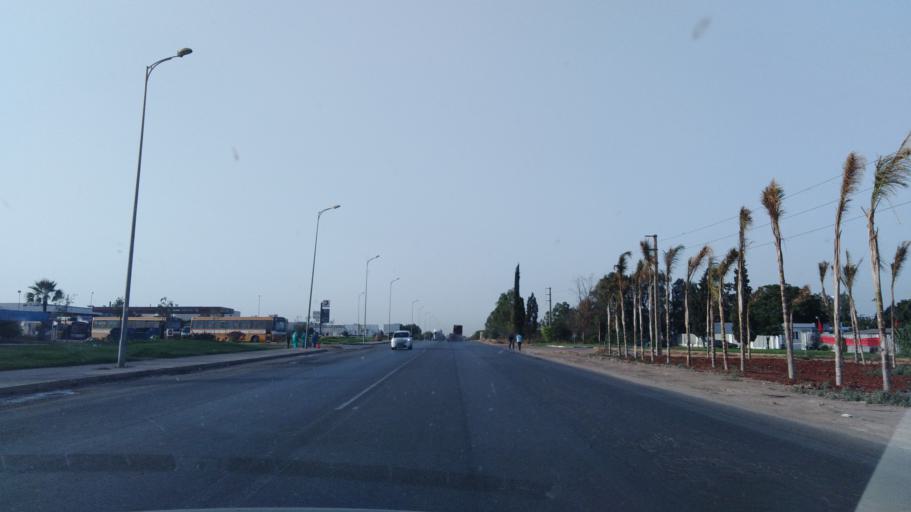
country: MA
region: Chaouia-Ouardigha
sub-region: Settat Province
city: Berrechid
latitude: 33.2459
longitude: -7.5861
